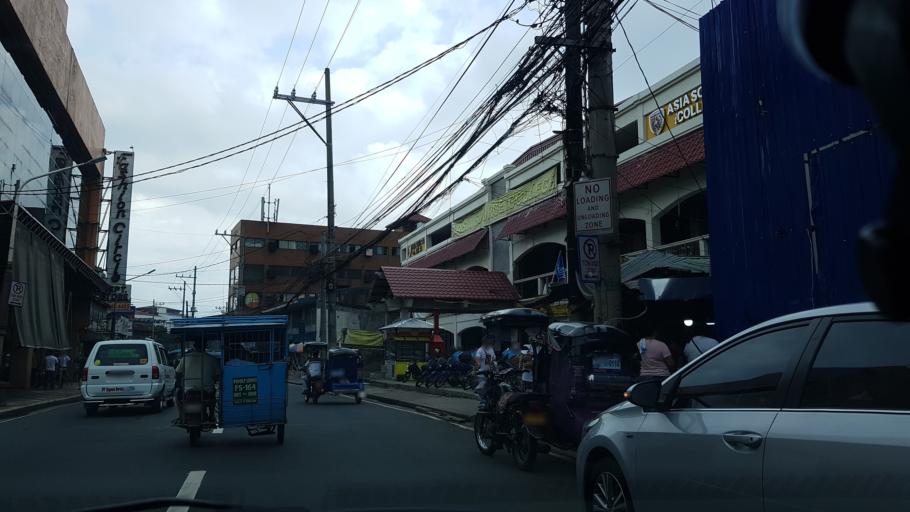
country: PH
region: Calabarzon
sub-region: Province of Rizal
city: Pateros
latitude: 14.5626
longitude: 121.0760
